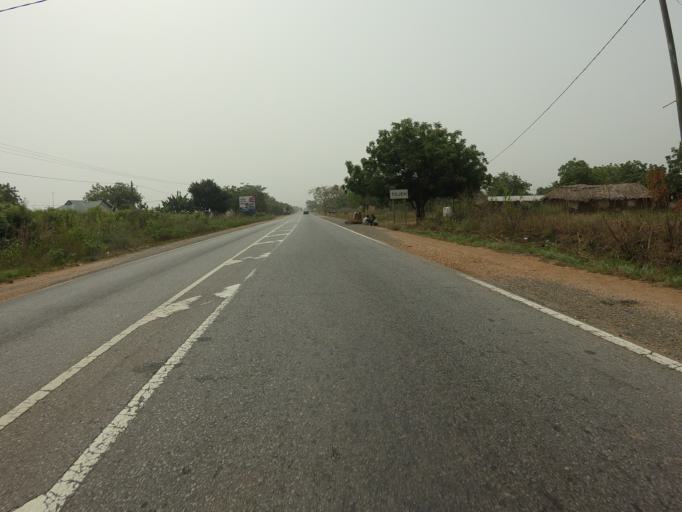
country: GH
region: Volta
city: Anloga
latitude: 5.9564
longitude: 0.5242
